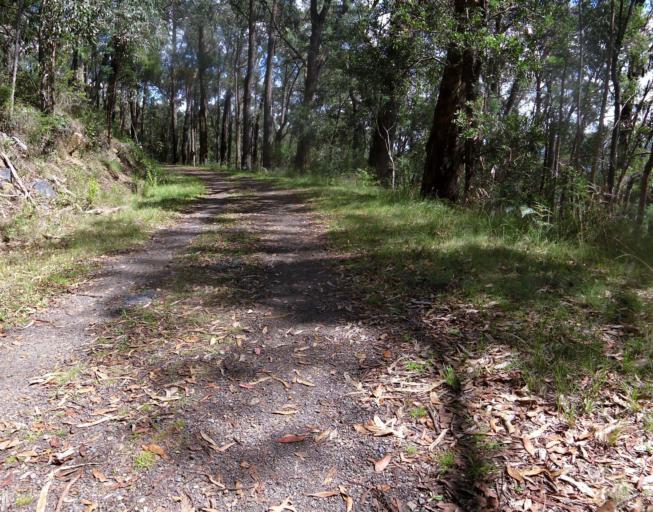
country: AU
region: Victoria
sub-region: Yarra Ranges
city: Montrose
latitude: -37.8200
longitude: 145.3576
